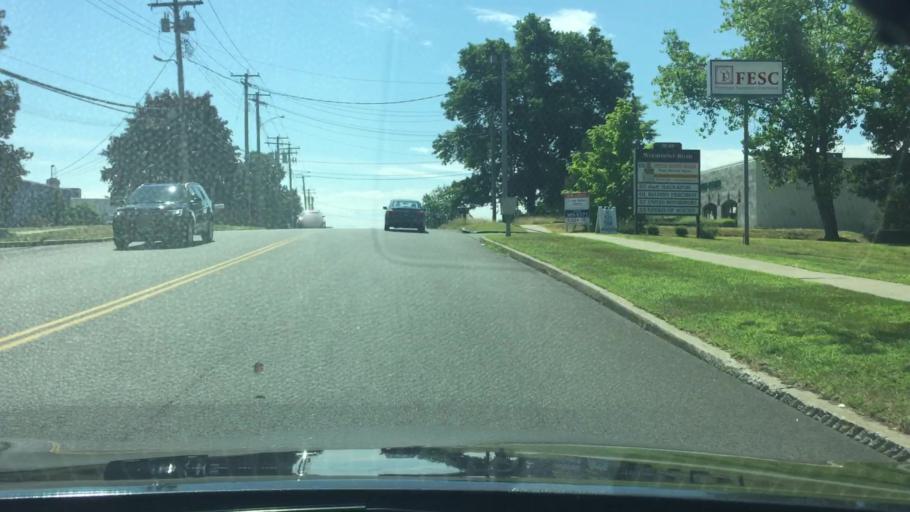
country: US
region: Connecticut
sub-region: New Haven County
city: Milford
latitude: 41.2411
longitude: -73.0256
